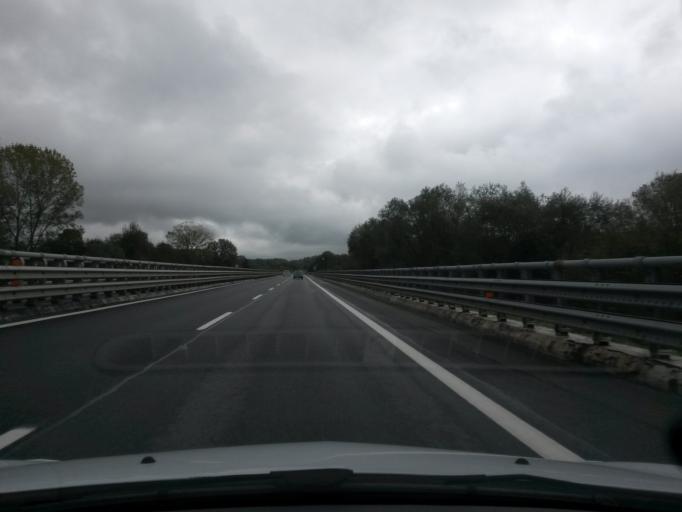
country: IT
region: Piedmont
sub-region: Provincia di Torino
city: Rosta
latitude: 45.0888
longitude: 7.4743
